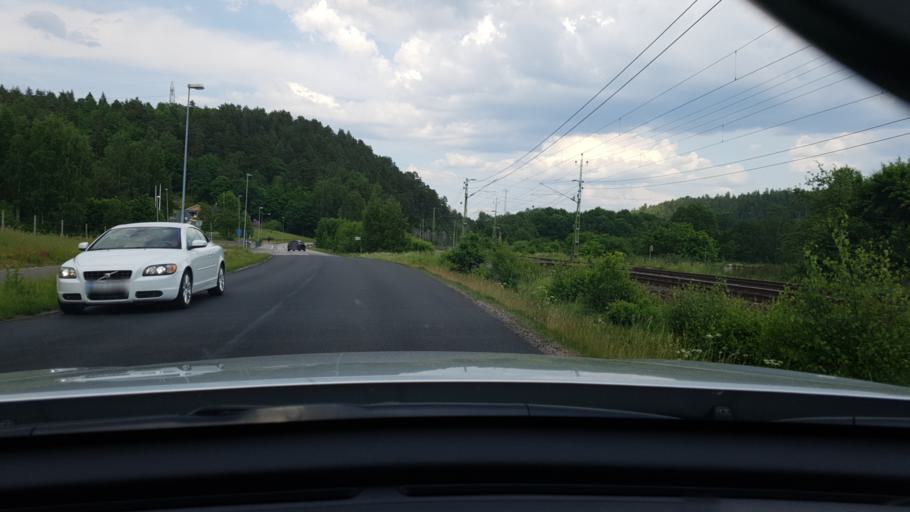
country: SE
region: Vaestra Goetaland
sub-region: Lerums Kommun
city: Stenkullen
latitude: 57.8005
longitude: 12.3340
